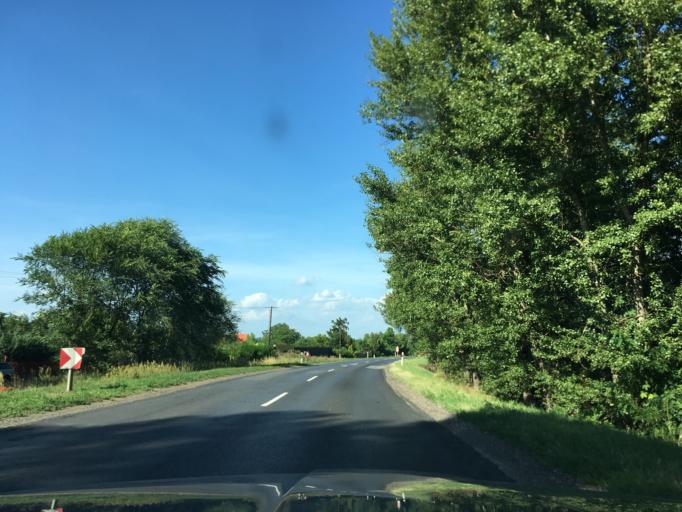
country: HU
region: Hajdu-Bihar
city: Debrecen
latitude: 47.5626
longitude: 21.6758
